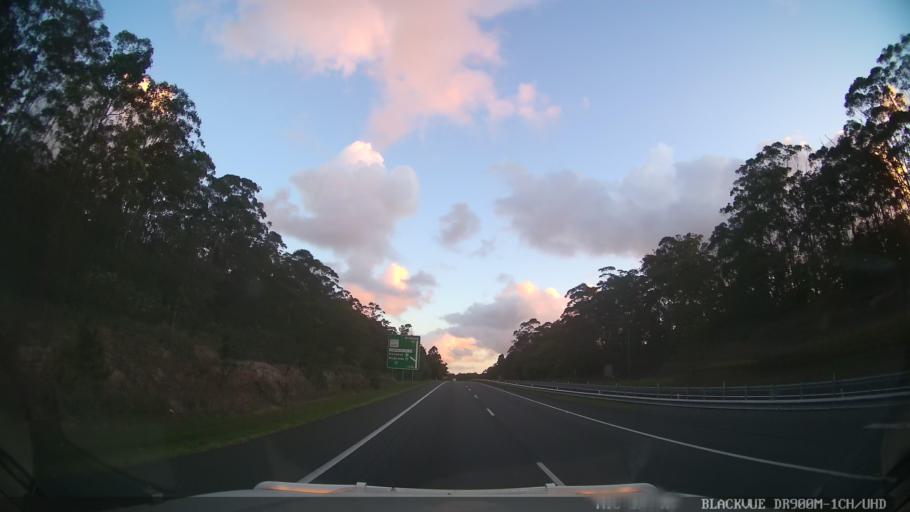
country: AU
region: Queensland
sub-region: Sunshine Coast
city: Twin Waters
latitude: -26.5975
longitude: 152.9719
